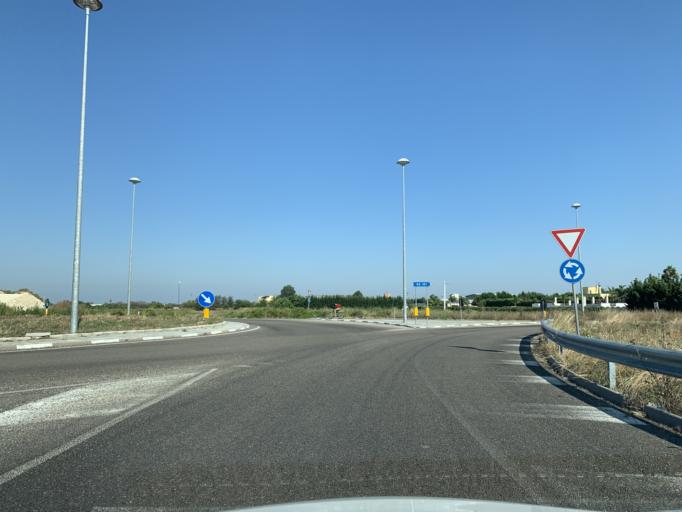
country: IT
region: Apulia
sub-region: Provincia di Lecce
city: Nardo
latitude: 40.1892
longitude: 18.0390
